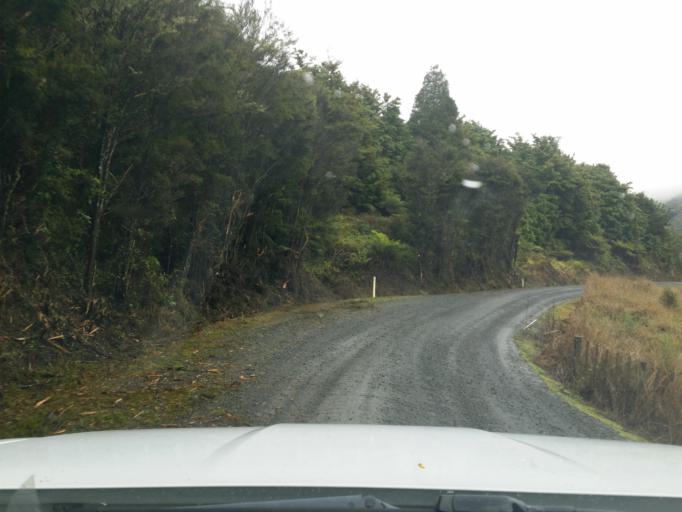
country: NZ
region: Northland
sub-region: Kaipara District
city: Dargaville
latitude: -35.7690
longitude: 173.9405
